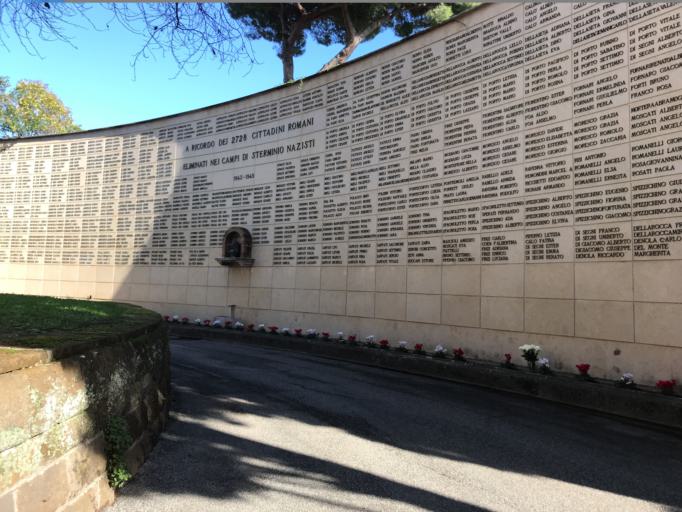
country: IT
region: Latium
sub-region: Citta metropolitana di Roma Capitale
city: Rome
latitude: 41.9003
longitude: 12.5281
